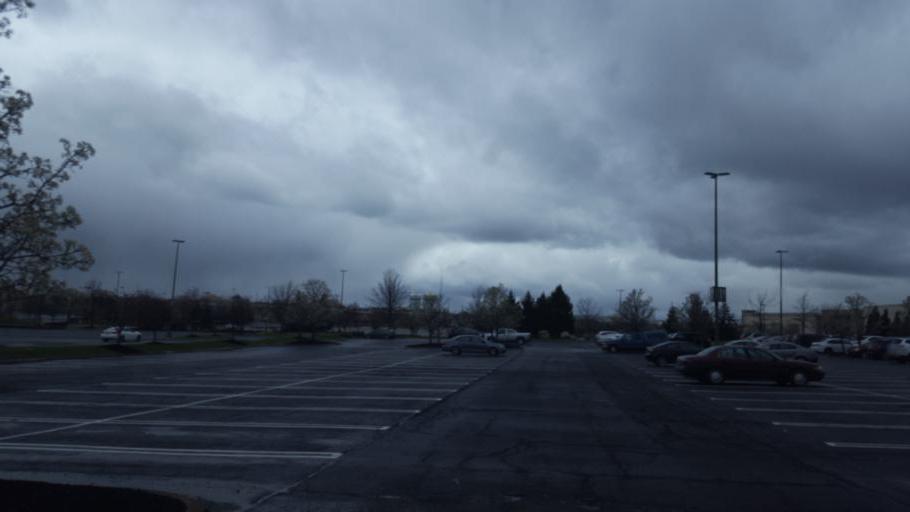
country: US
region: Ohio
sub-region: Franklin County
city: Westerville
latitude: 40.1439
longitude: -82.9804
